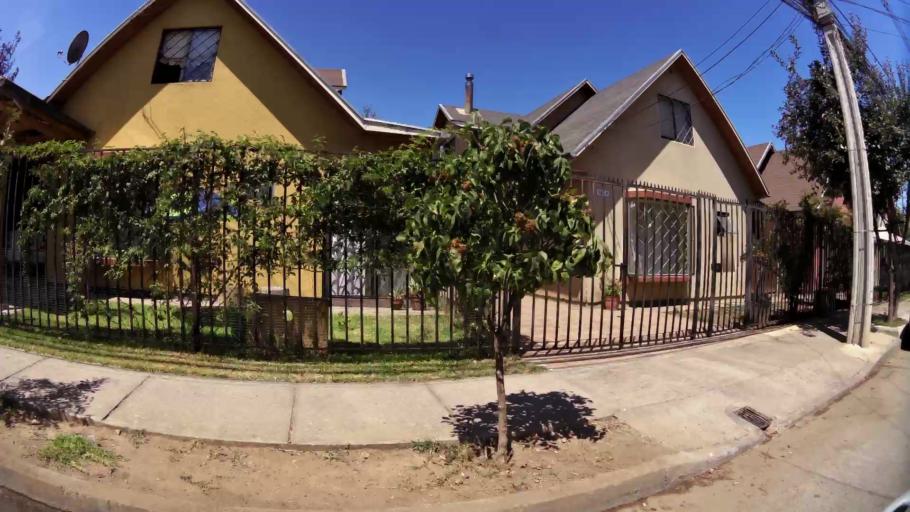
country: CL
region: Maule
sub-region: Provincia de Talca
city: Talca
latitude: -35.4277
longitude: -71.6214
